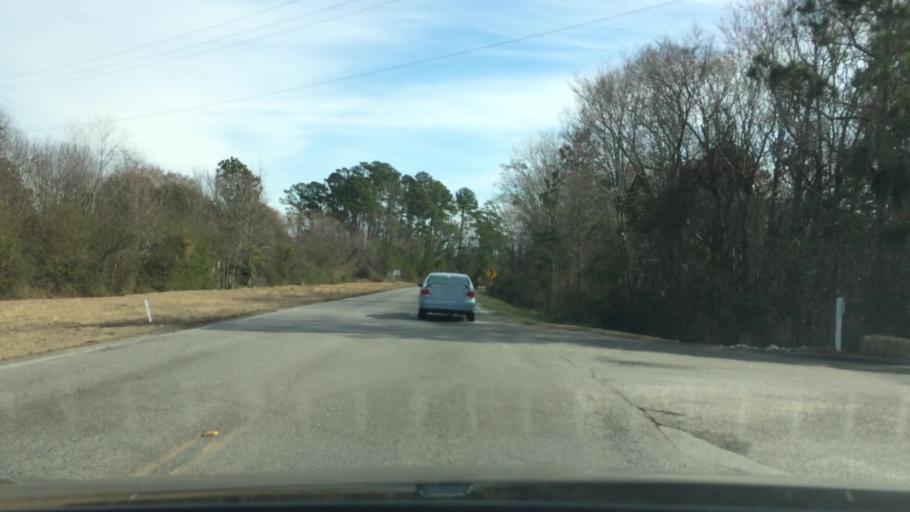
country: US
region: South Carolina
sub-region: Horry County
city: Socastee
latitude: 33.6783
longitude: -78.9707
